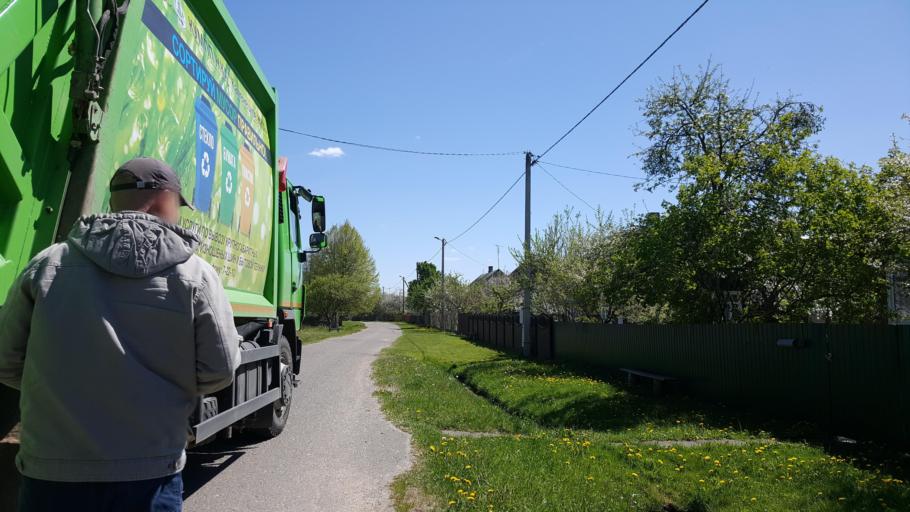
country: BY
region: Brest
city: Kamyanyuki
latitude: 52.5610
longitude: 23.8060
